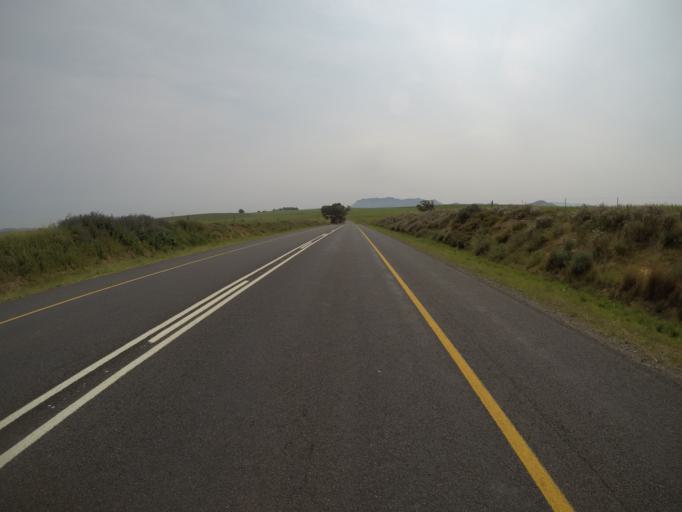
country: ZA
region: Western Cape
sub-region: West Coast District Municipality
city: Malmesbury
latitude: -33.5182
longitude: 18.8462
